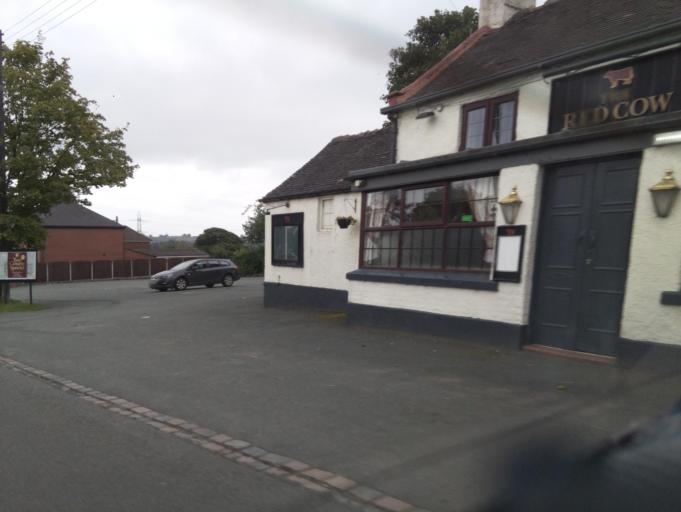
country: GB
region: England
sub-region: Staffordshire
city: Cheddleton
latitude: 53.0258
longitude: -2.0827
